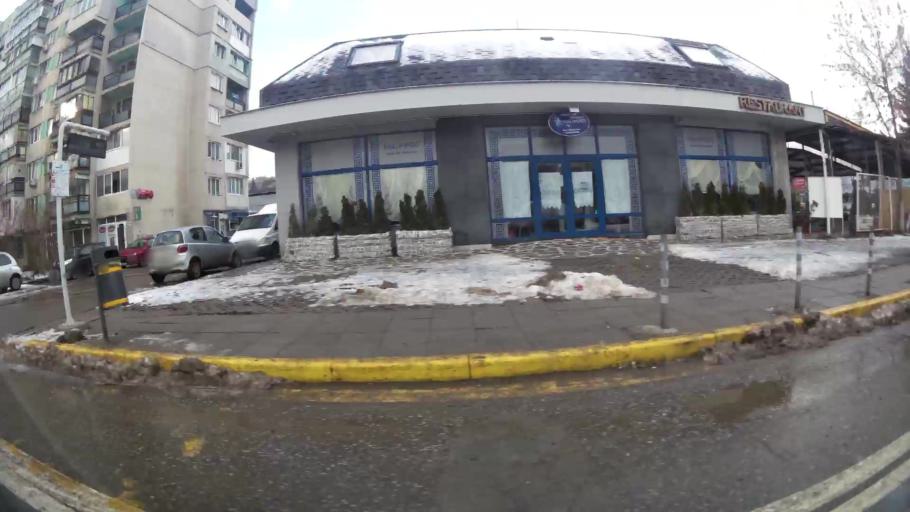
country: BG
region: Sofia-Capital
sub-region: Stolichna Obshtina
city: Sofia
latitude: 42.7018
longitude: 23.2854
